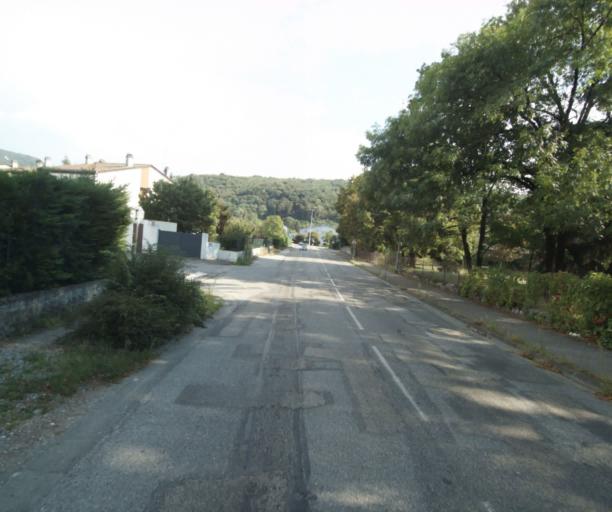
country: FR
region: Rhone-Alpes
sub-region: Departement de l'Isere
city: Echirolles
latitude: 45.1446
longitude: 5.7280
